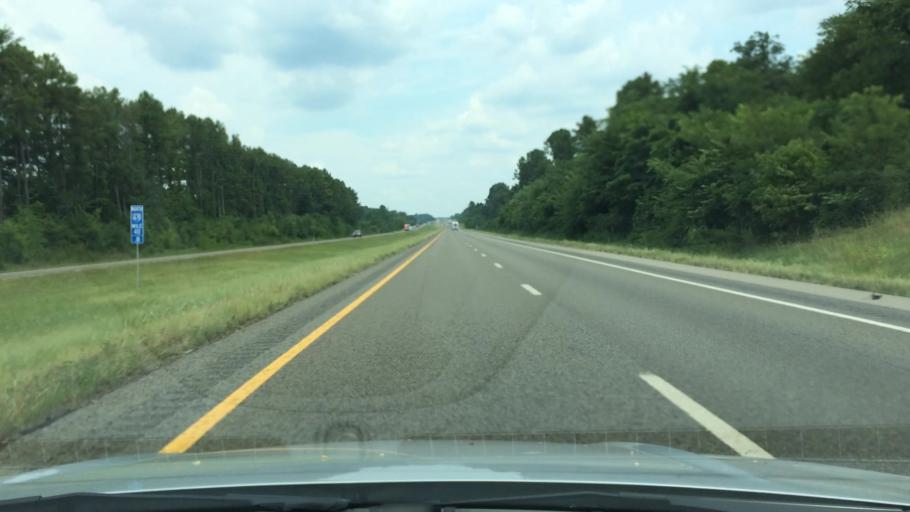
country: US
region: Tennessee
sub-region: Maury County
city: Columbia
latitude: 35.5672
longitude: -86.9057
